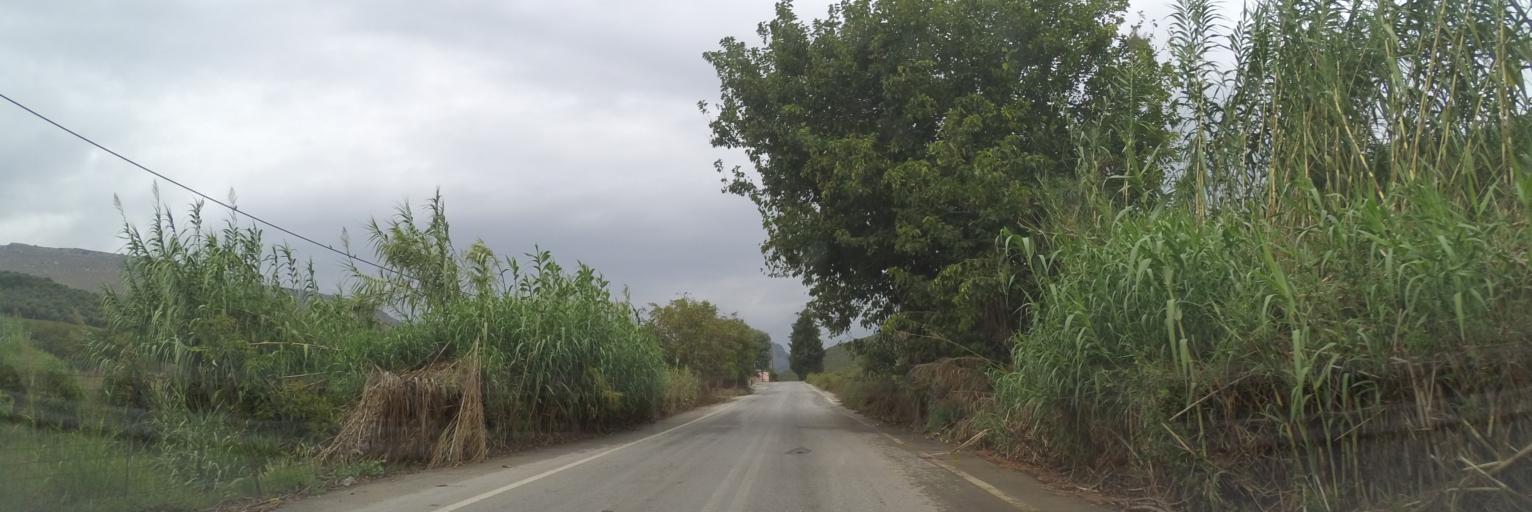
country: GR
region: Crete
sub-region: Nomos Rethymnis
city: Agia Foteini
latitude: 35.2891
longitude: 24.5625
